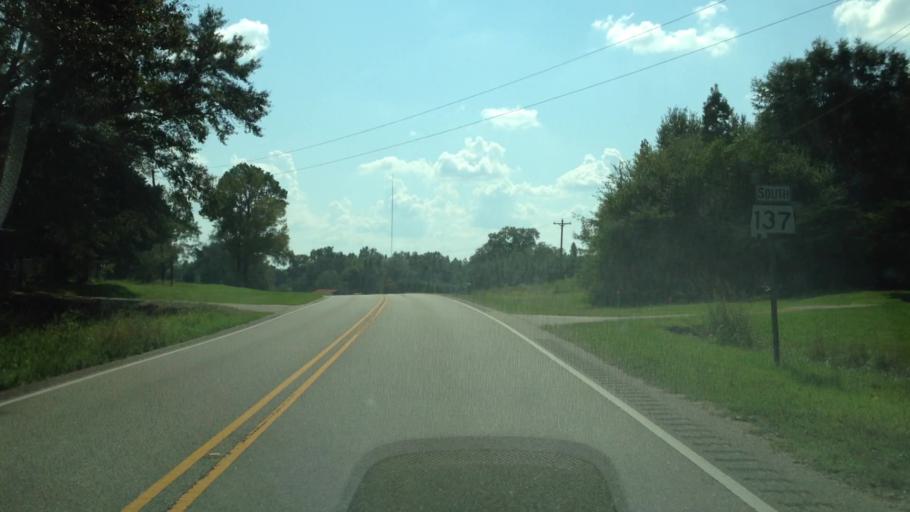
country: US
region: Florida
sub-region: Okaloosa County
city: Crestview
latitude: 31.0331
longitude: -86.6072
